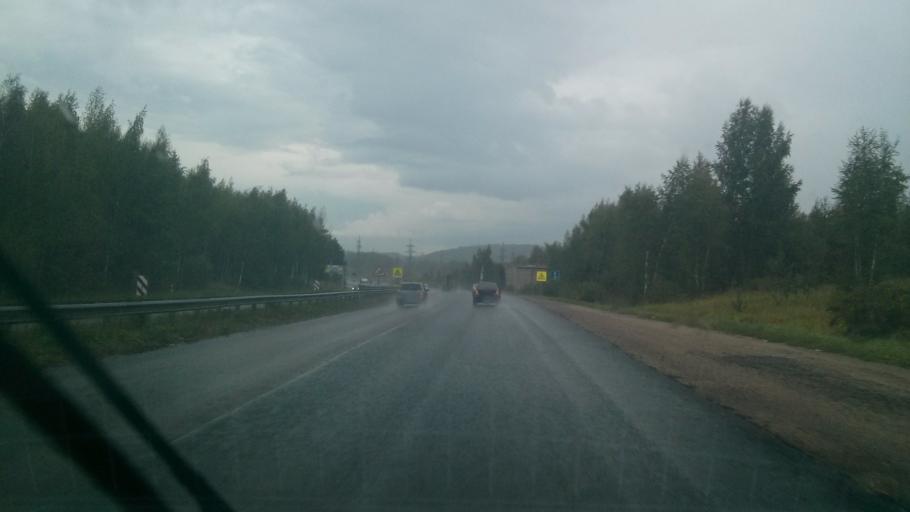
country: RU
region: Nizjnij Novgorod
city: Afonino
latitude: 56.2317
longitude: 44.0682
